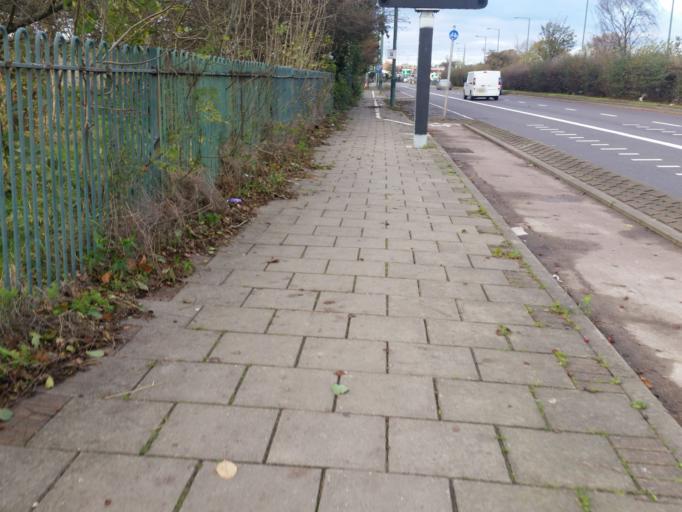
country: GB
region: England
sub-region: Greater London
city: Harringay
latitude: 51.6106
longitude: -0.0861
